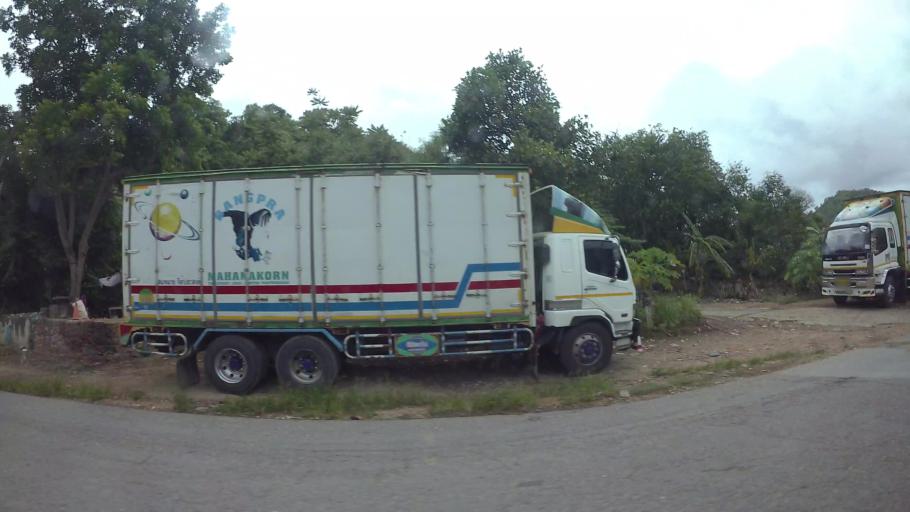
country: TH
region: Chon Buri
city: Si Racha
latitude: 13.2004
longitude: 100.9547
